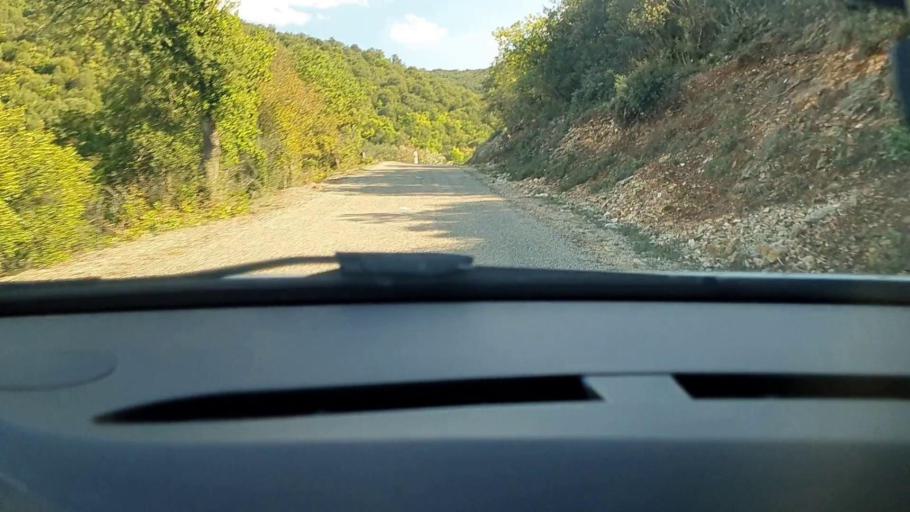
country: FR
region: Languedoc-Roussillon
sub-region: Departement du Gard
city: Saint-Ambroix
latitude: 44.2144
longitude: 4.2965
